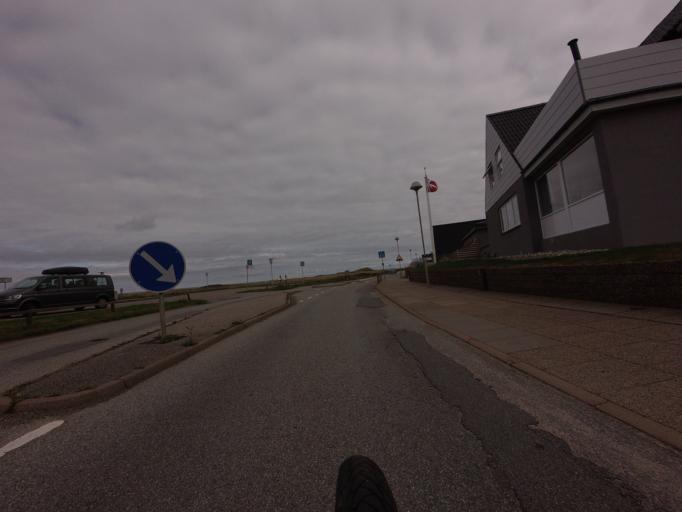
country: DK
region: North Denmark
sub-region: Hjorring Kommune
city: Hirtshals
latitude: 57.5882
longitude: 9.9481
